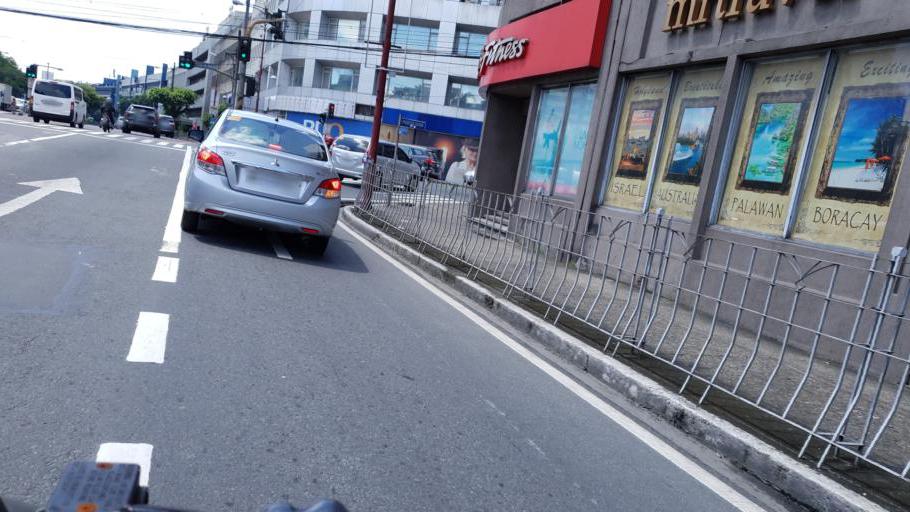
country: PH
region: Metro Manila
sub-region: Makati City
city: Makati City
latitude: 14.5595
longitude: 121.0313
